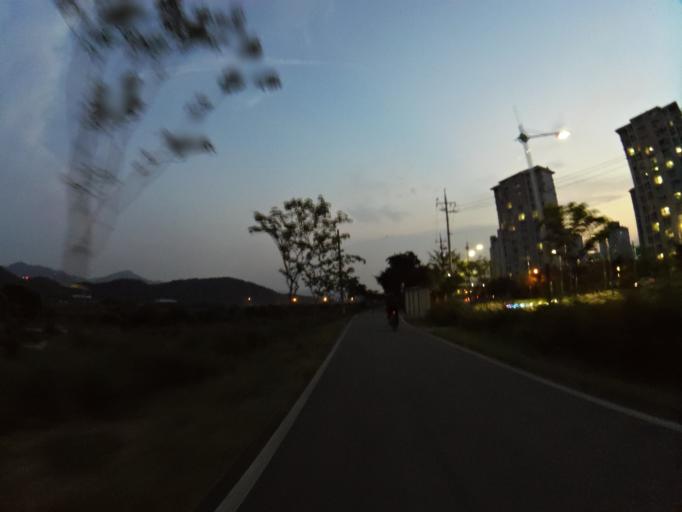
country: KR
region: Gyeongsangbuk-do
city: Gyeongsan-si
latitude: 35.8593
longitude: 128.7049
